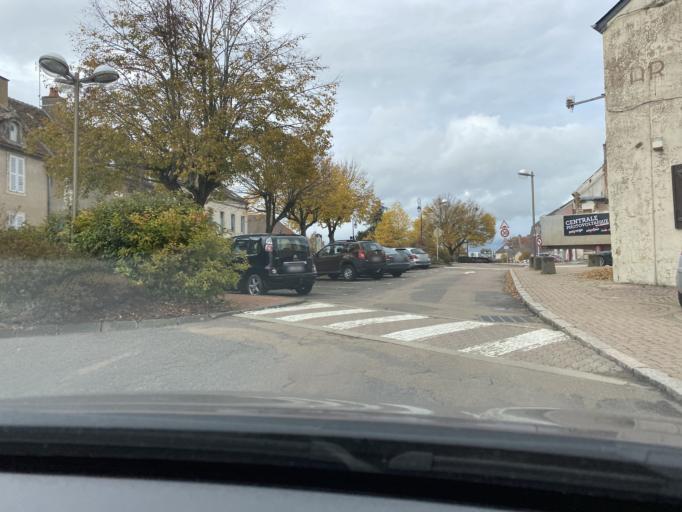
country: FR
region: Bourgogne
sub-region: Departement de la Cote-d'Or
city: Saulieu
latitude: 47.2815
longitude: 4.2282
